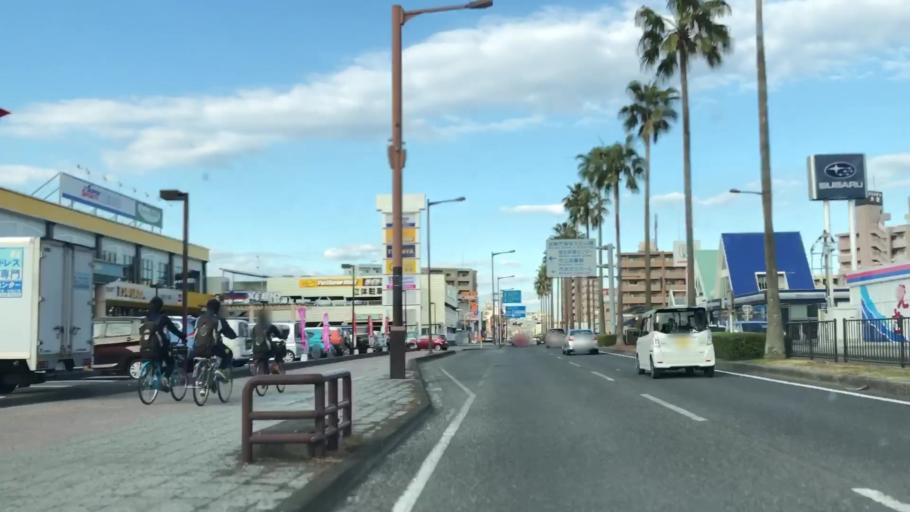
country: JP
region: Miyazaki
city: Miyazaki-shi
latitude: 31.8957
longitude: 131.4171
